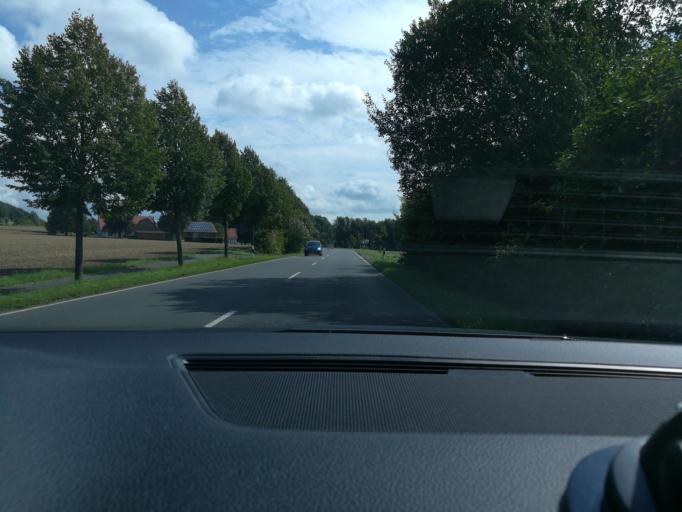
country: DE
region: North Rhine-Westphalia
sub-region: Regierungsbezirk Detmold
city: Hille
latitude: 52.2736
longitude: 8.7348
